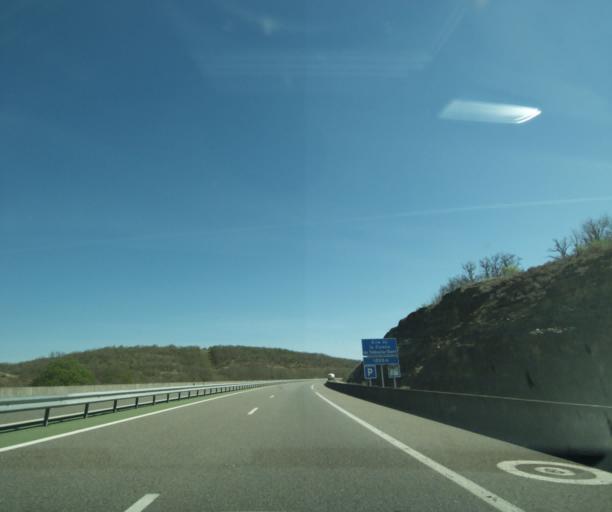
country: FR
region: Midi-Pyrenees
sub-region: Departement du Lot
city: Lalbenque
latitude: 44.4127
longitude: 1.5201
